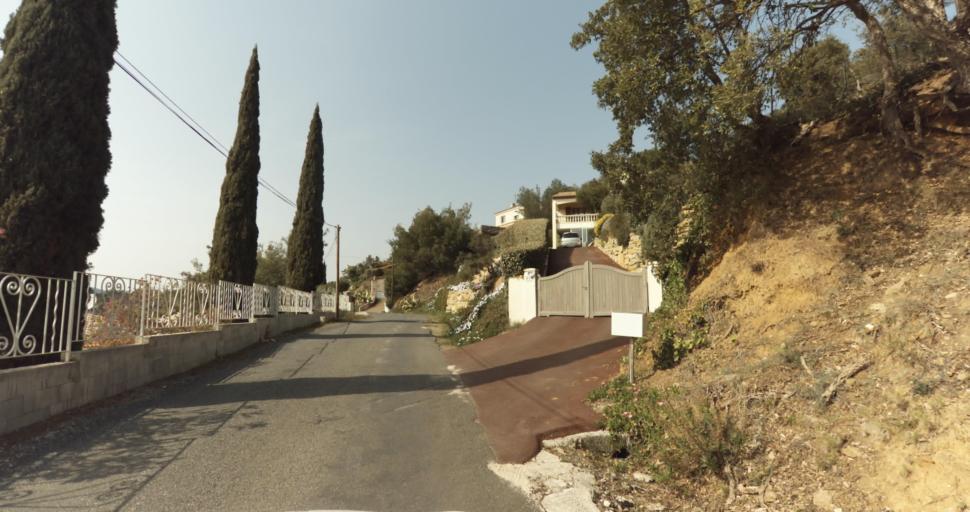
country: FR
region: Provence-Alpes-Cote d'Azur
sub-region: Departement du Var
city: Bormes-les-Mimosas
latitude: 43.1478
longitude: 6.3286
